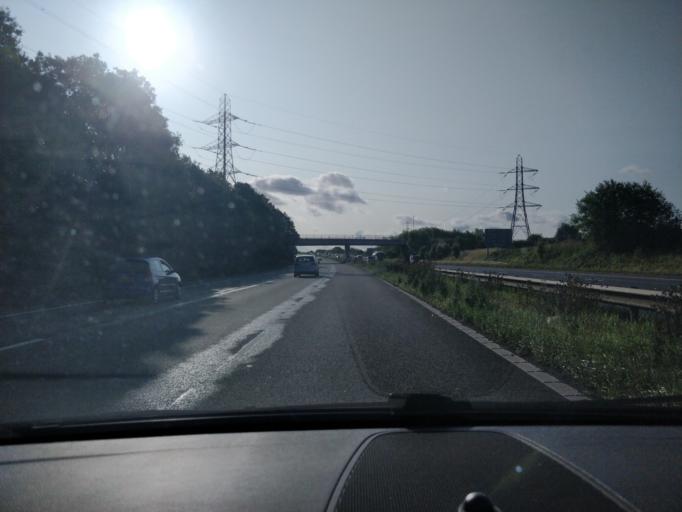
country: GB
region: England
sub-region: Sefton
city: Melling
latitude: 53.4856
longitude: -2.9300
